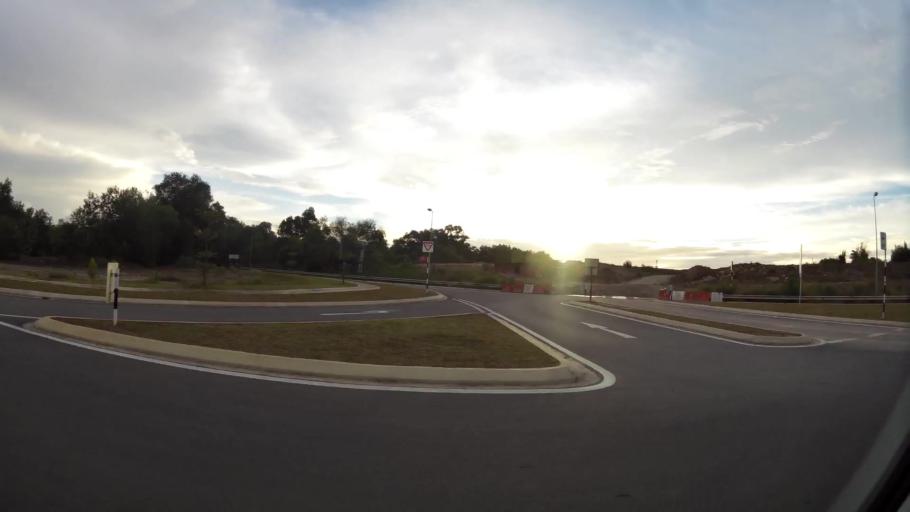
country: BN
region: Brunei and Muara
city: Bandar Seri Begawan
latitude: 4.9948
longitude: 114.9844
